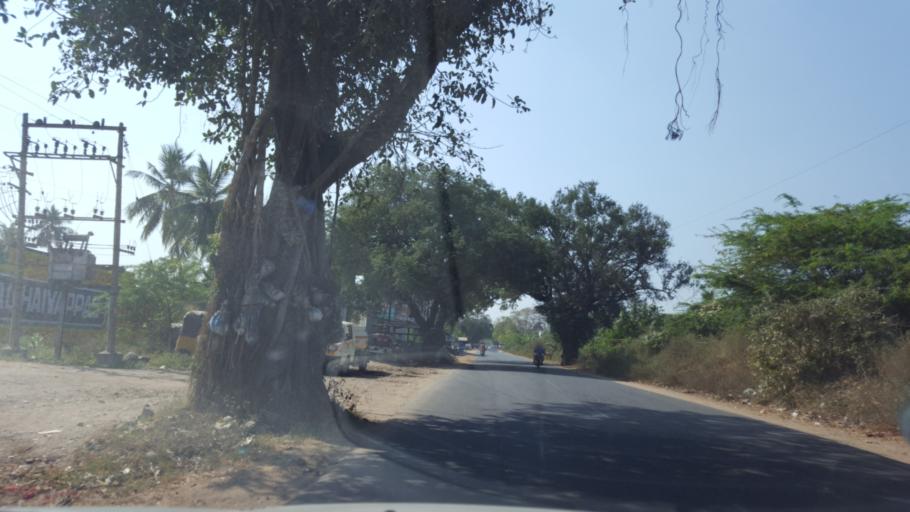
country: IN
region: Tamil Nadu
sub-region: Kancheepuram
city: Kanchipuram
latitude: 12.8572
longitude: 79.6823
